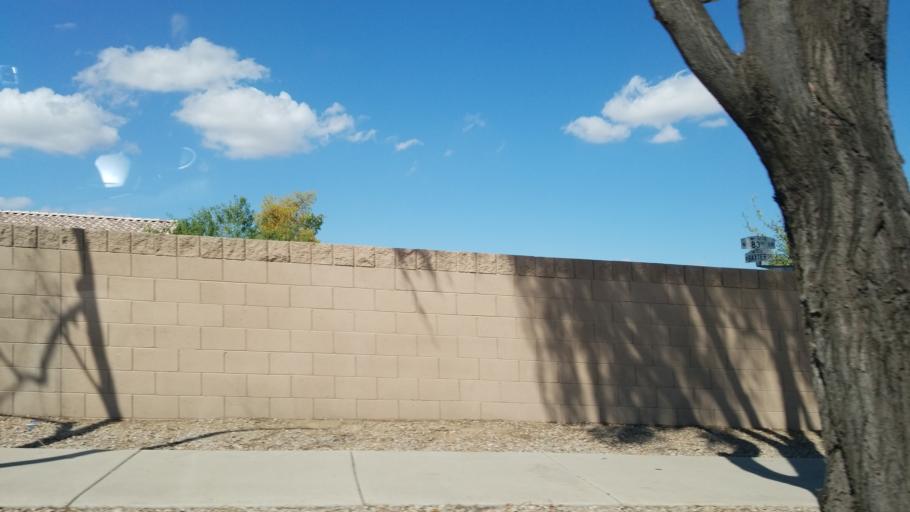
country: US
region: Arizona
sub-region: Maricopa County
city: Tolleson
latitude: 33.5033
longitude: -112.2379
